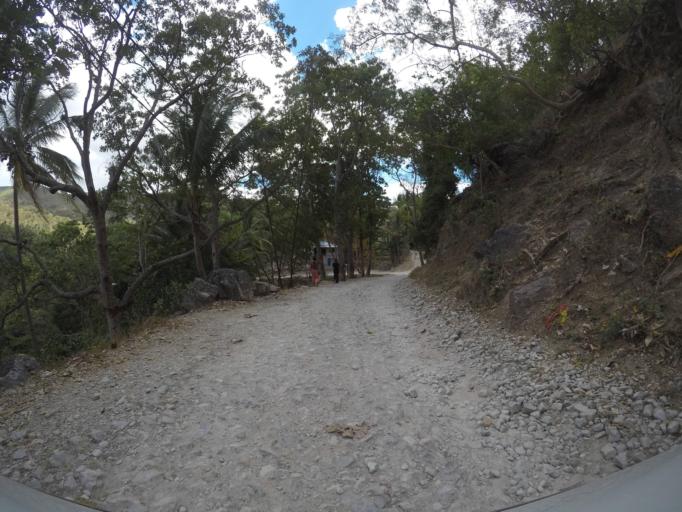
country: TL
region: Baucau
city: Baucau
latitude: -8.5246
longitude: 126.6936
